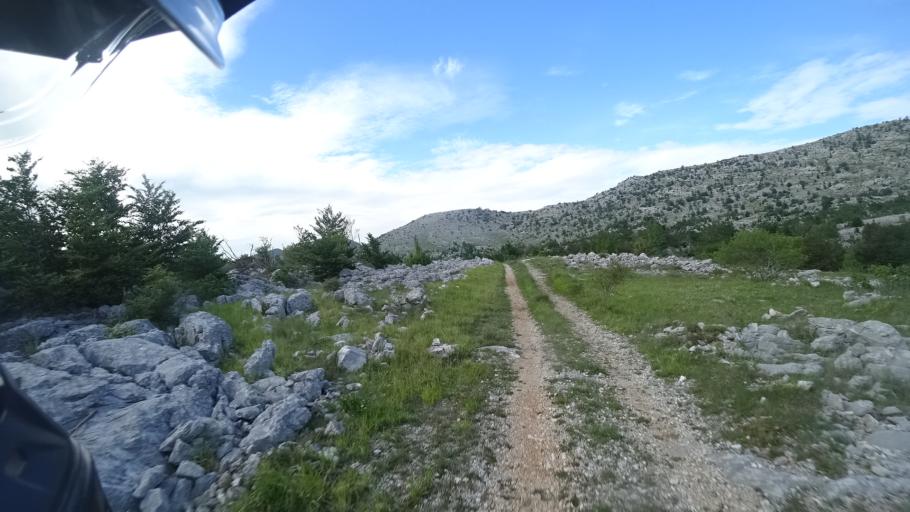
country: HR
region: Splitsko-Dalmatinska
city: Hrvace
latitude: 43.8062
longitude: 16.4337
